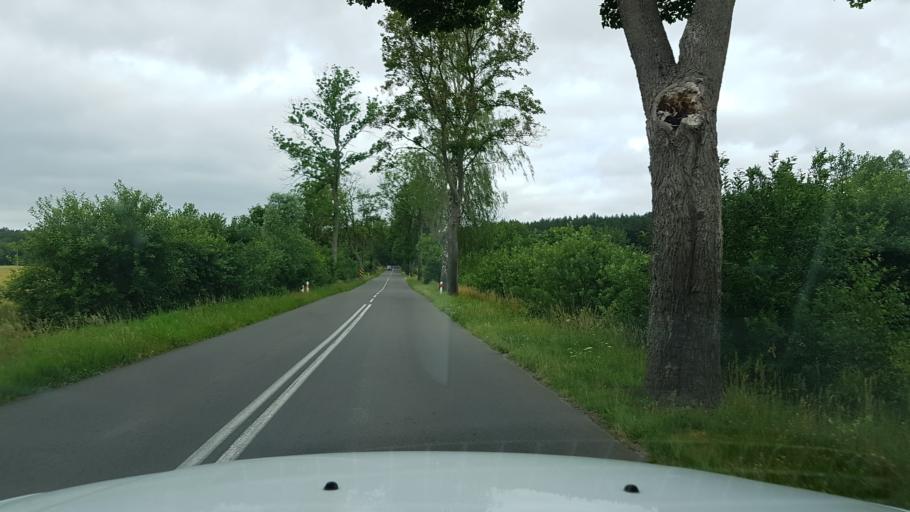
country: PL
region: West Pomeranian Voivodeship
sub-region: Powiat gryficki
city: Cerkwica
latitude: 53.9261
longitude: 15.1014
